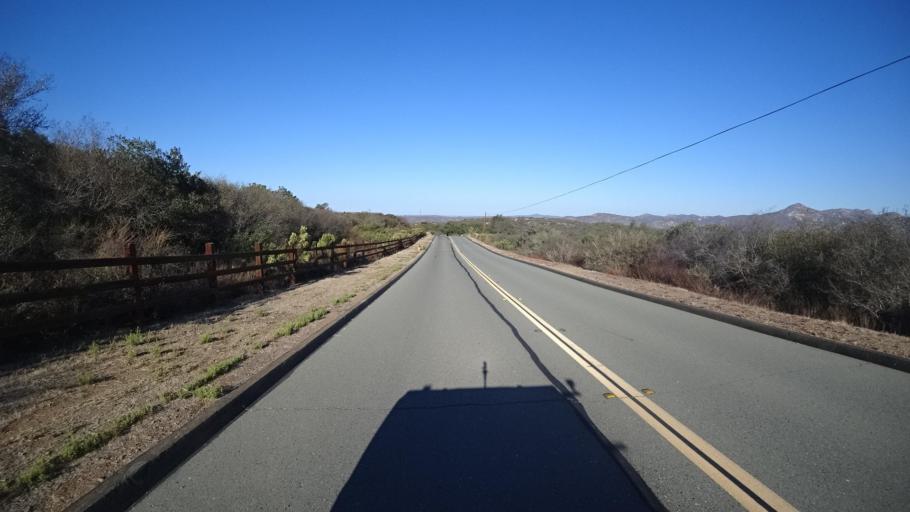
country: US
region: California
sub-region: San Diego County
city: Eucalyptus Hills
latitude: 32.9059
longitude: -116.9103
